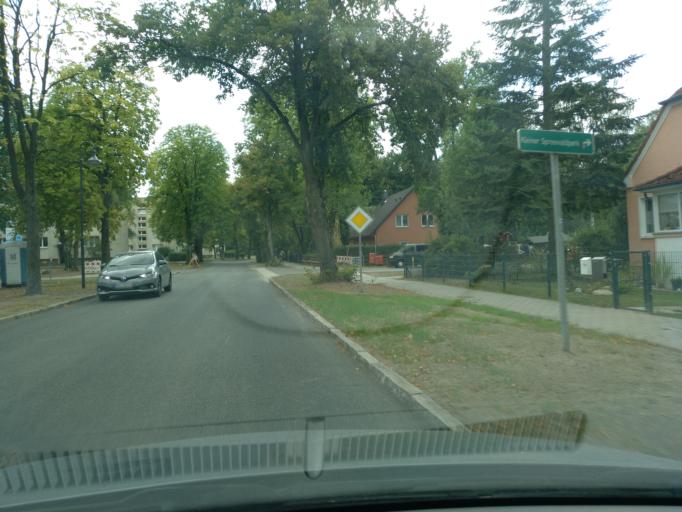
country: DE
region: Brandenburg
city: Schoneiche
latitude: 52.4743
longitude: 13.6987
